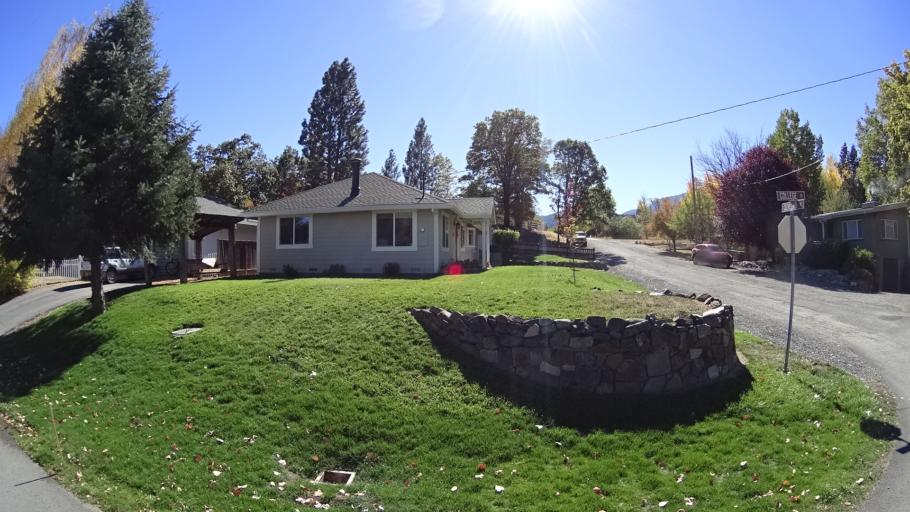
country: US
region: California
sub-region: Siskiyou County
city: Yreka
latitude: 41.4569
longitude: -122.9002
